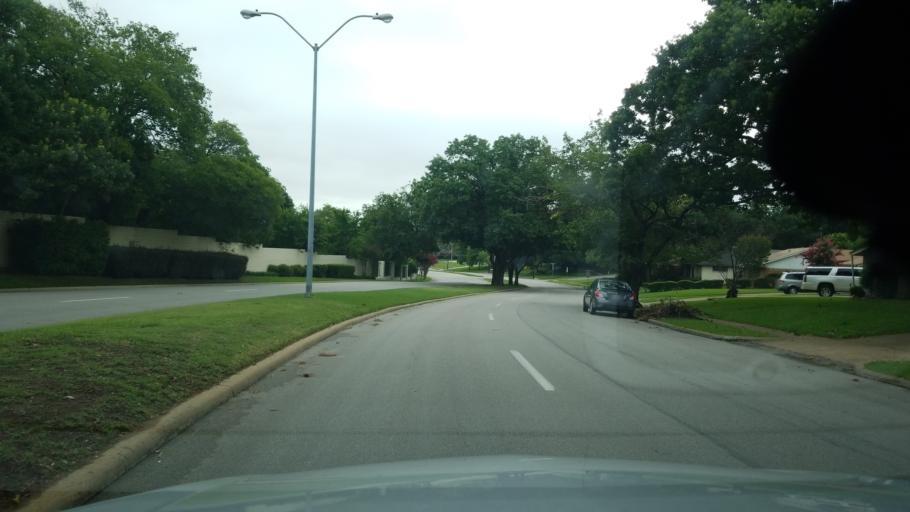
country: US
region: Texas
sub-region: Dallas County
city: Irving
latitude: 32.8533
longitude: -96.9470
